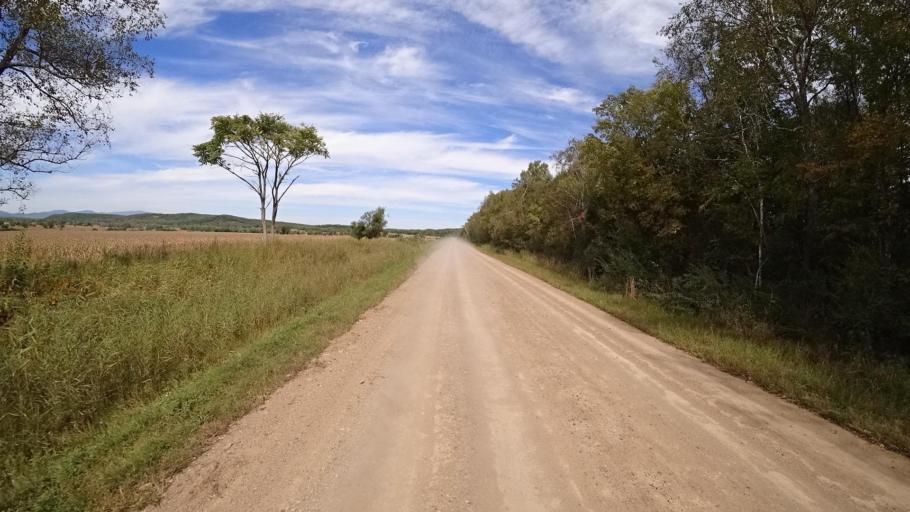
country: RU
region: Primorskiy
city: Yakovlevka
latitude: 44.5828
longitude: 133.5999
